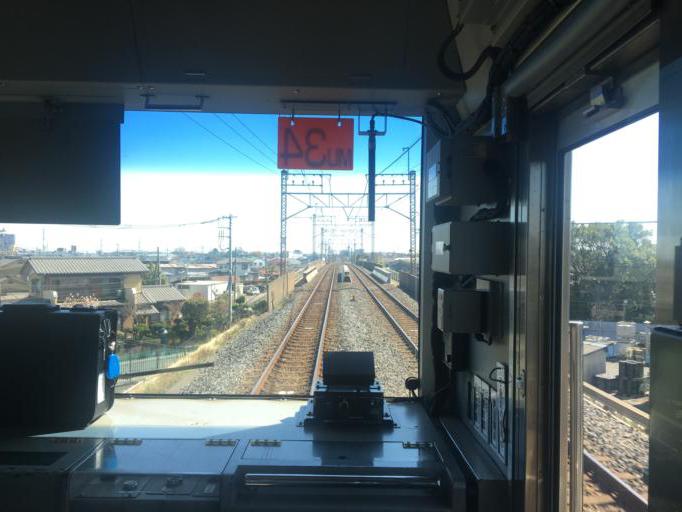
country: JP
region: Saitama
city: Koshigaya
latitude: 35.8753
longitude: 139.7591
